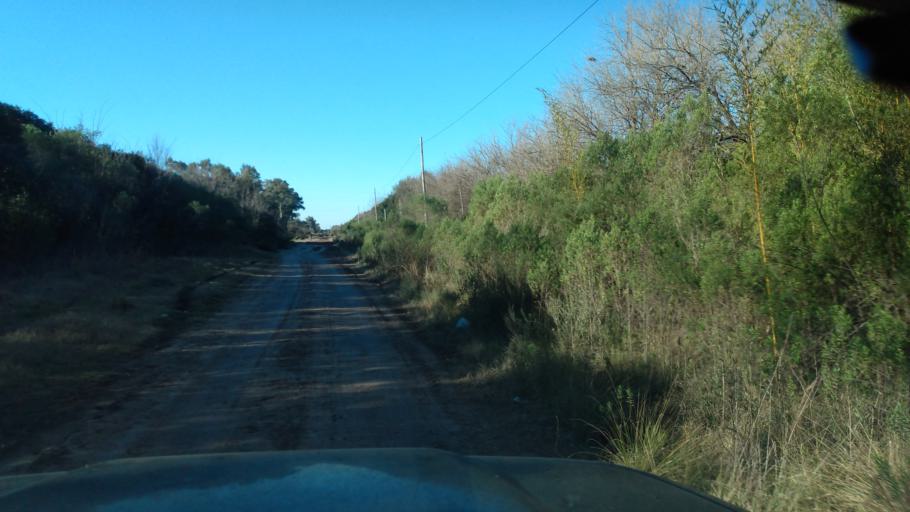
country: AR
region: Buenos Aires
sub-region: Partido de Lujan
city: Lujan
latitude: -34.5553
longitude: -59.1507
